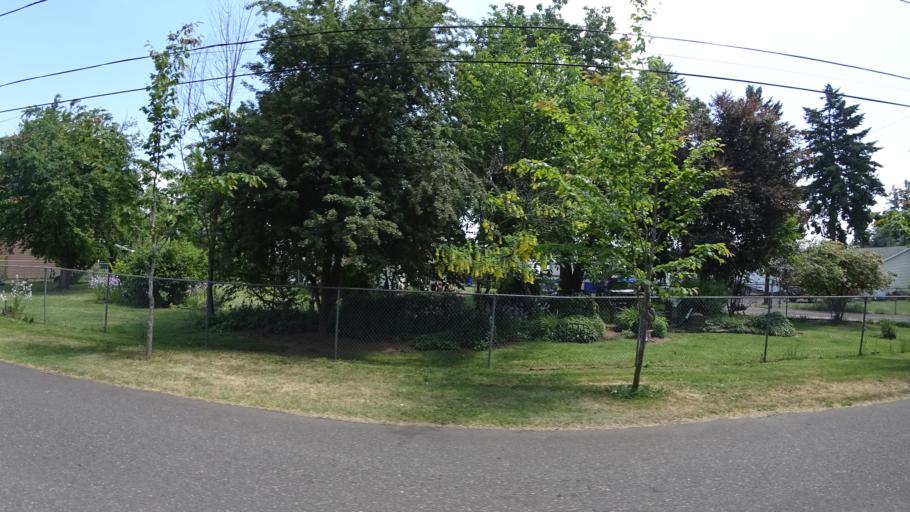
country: US
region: Oregon
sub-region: Multnomah County
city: Fairview
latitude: 45.5352
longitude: -122.5038
